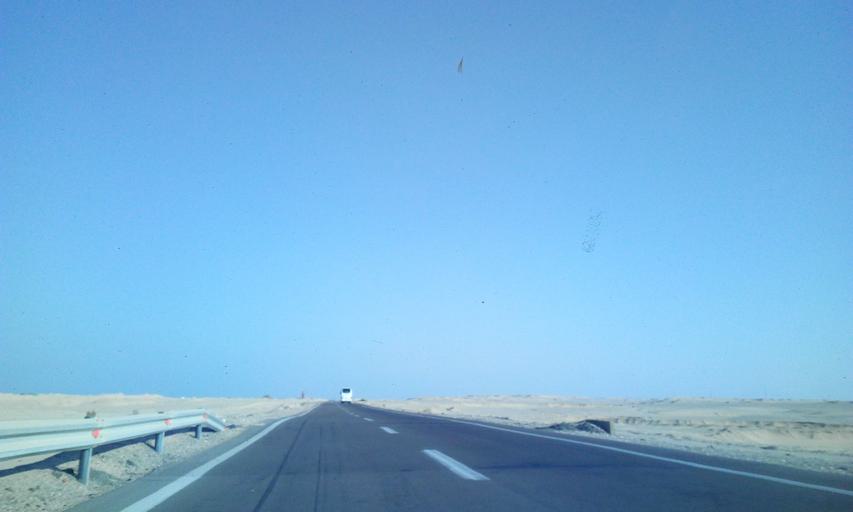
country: EG
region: As Suways
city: Ain Sukhna
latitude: 28.8636
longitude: 32.6756
